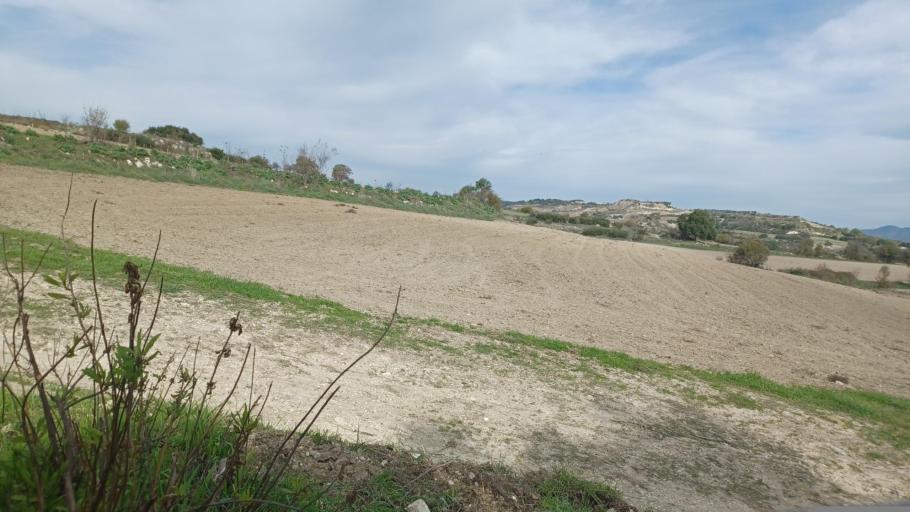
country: CY
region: Pafos
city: Mesogi
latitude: 34.8568
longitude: 32.5359
